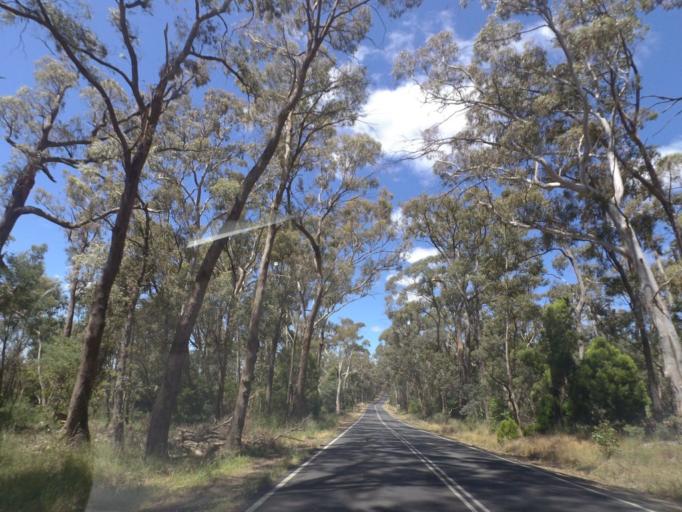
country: AU
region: Victoria
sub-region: Mount Alexander
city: Castlemaine
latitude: -37.2885
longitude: 144.2719
